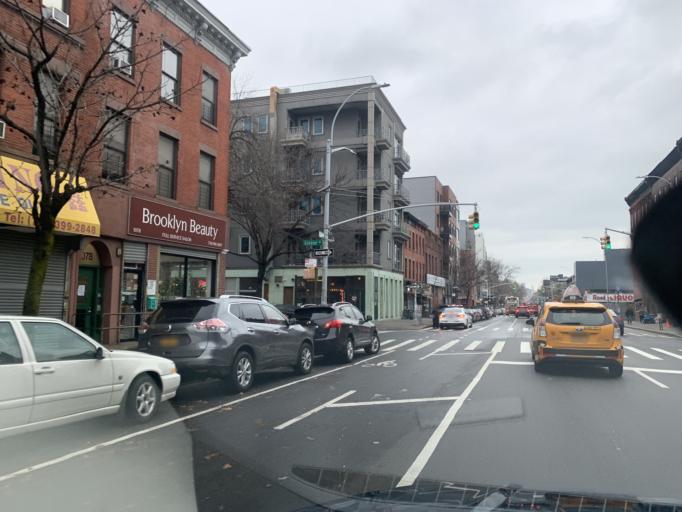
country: US
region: New York
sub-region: Kings County
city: Brooklyn
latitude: 40.6877
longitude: -73.9548
